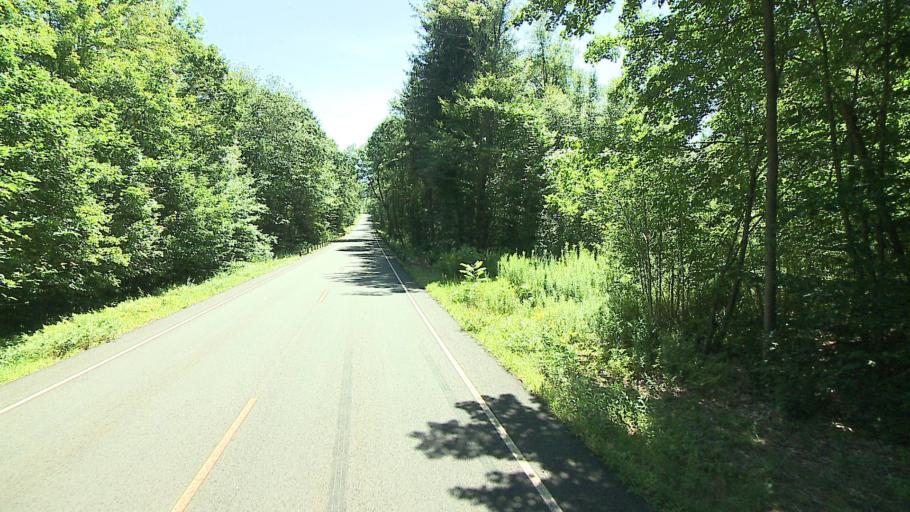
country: US
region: Connecticut
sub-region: Litchfield County
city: New Hartford Center
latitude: 41.9730
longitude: -72.9805
